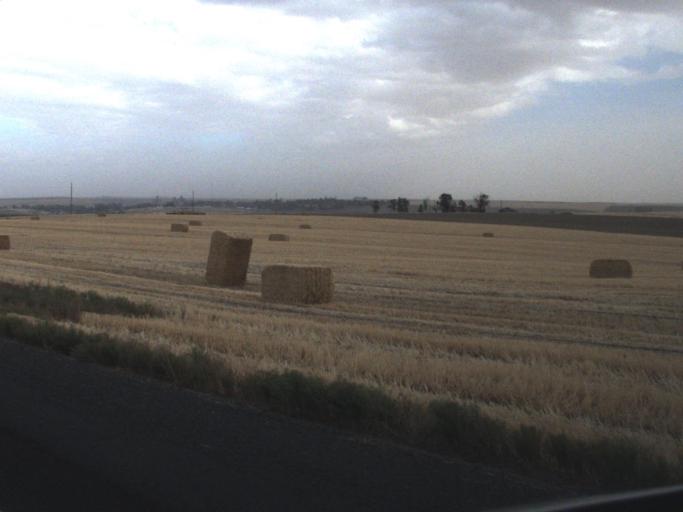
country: US
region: Washington
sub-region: Lincoln County
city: Davenport
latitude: 47.4630
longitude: -118.3024
